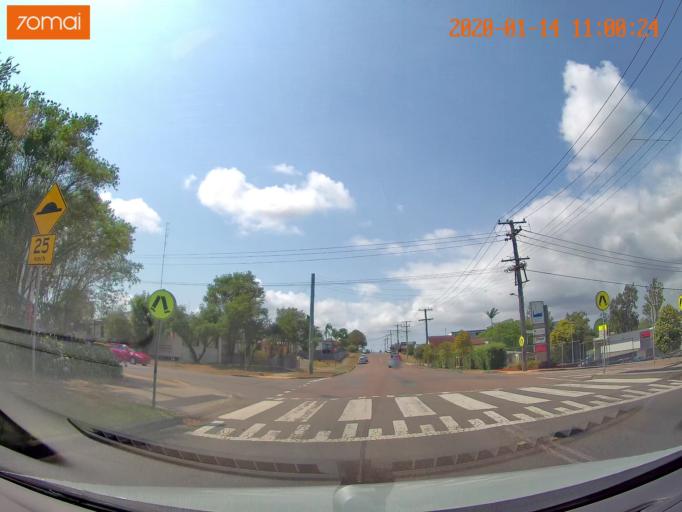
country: AU
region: New South Wales
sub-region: Lake Macquarie Shire
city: Dora Creek
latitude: -33.1055
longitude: 151.4886
